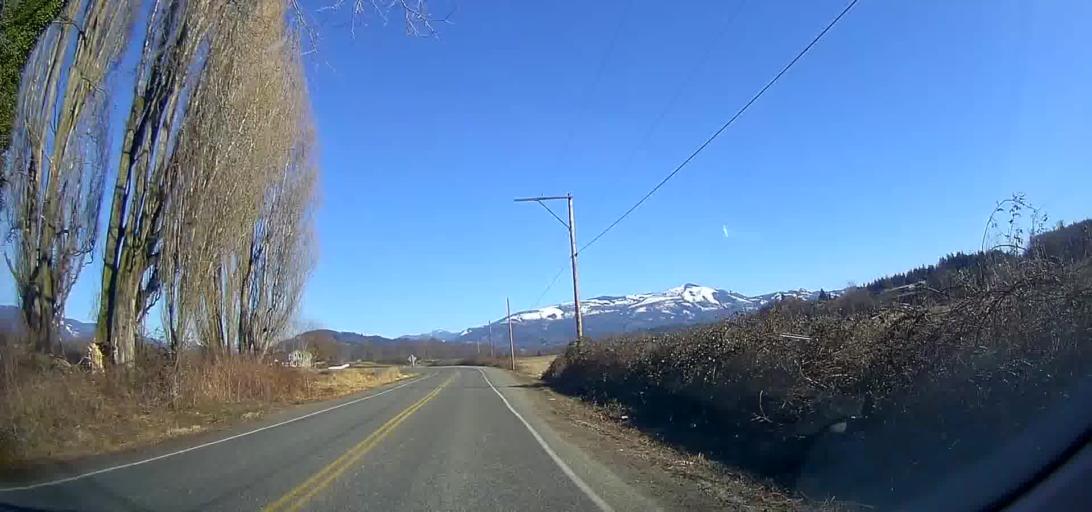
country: US
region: Washington
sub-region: Skagit County
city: Burlington
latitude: 48.4647
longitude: -122.3008
